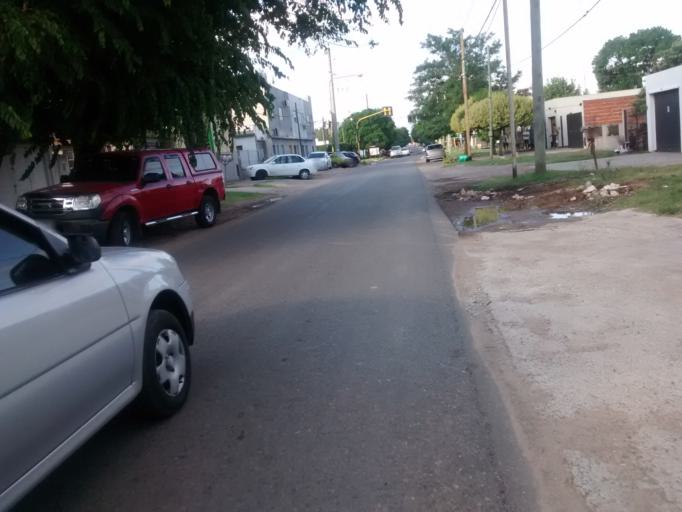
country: AR
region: Buenos Aires
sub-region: Partido de La Plata
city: La Plata
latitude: -34.9435
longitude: -57.9265
